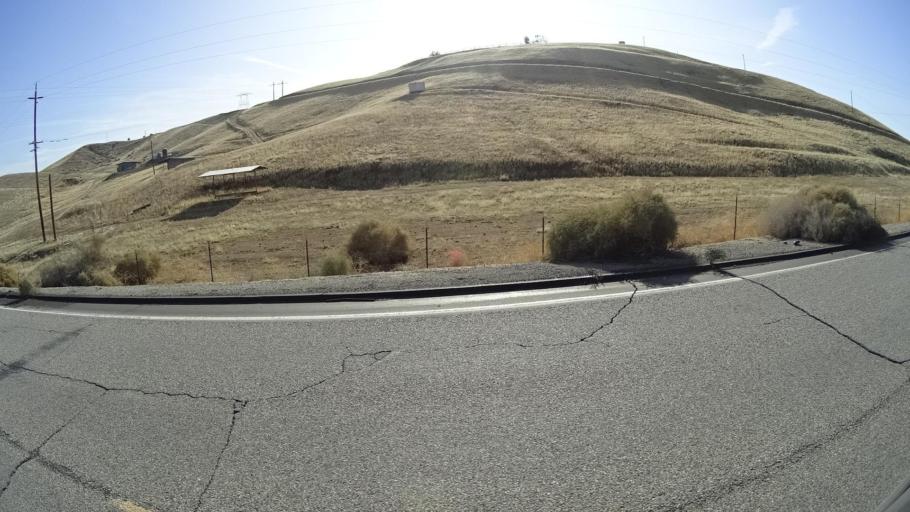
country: US
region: California
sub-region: Kern County
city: Oildale
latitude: 35.5007
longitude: -118.9931
